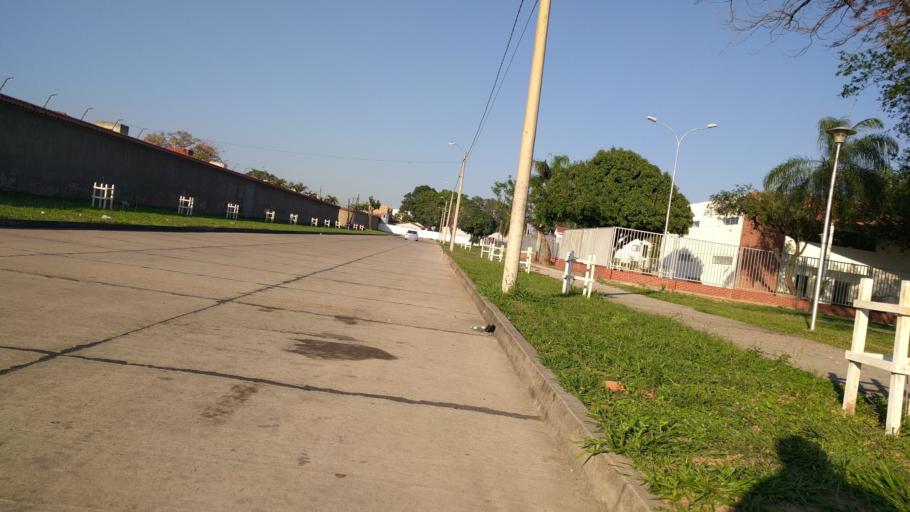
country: BO
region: Santa Cruz
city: Santa Cruz de la Sierra
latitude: -17.8127
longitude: -63.1655
